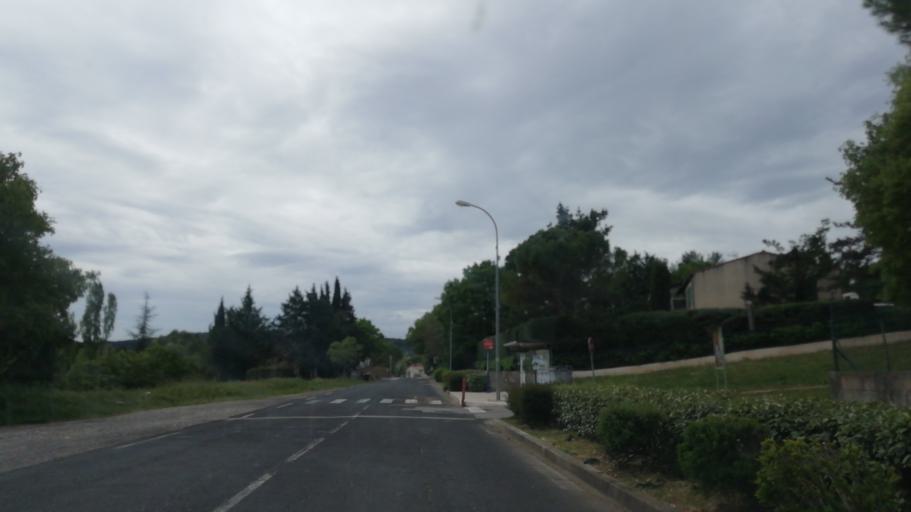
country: FR
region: Languedoc-Roussillon
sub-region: Departement de l'Herault
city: Saint-Martin-de-Londres
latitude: 43.7957
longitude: 3.7337
